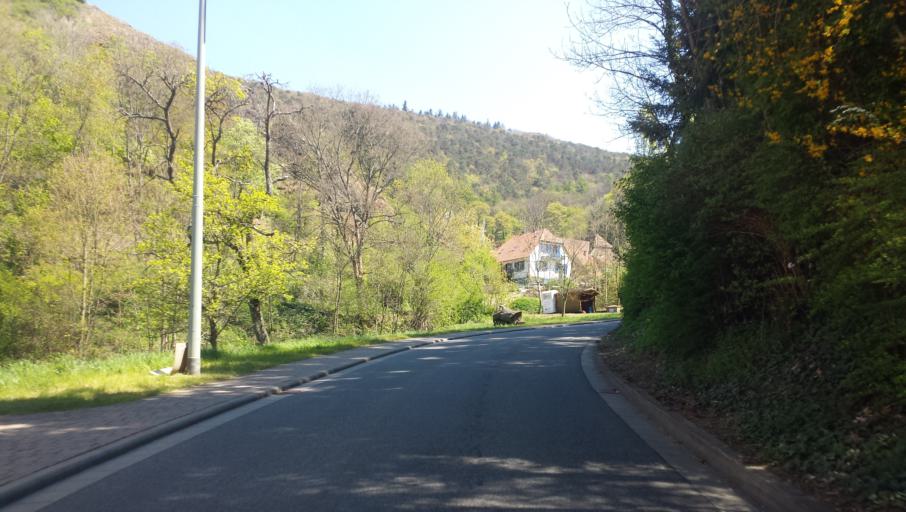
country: DE
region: Rheinland-Pfalz
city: Falkenstein
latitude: 49.6076
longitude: 7.8712
